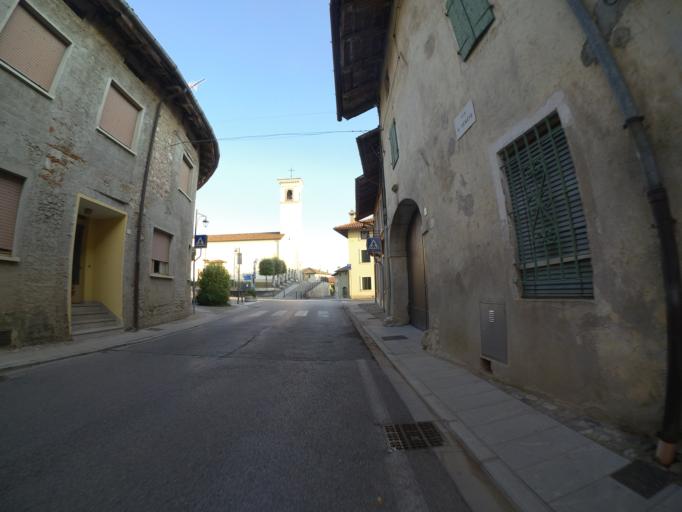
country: IT
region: Friuli Venezia Giulia
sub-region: Provincia di Udine
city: Campoformido
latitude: 46.0074
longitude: 13.1434
